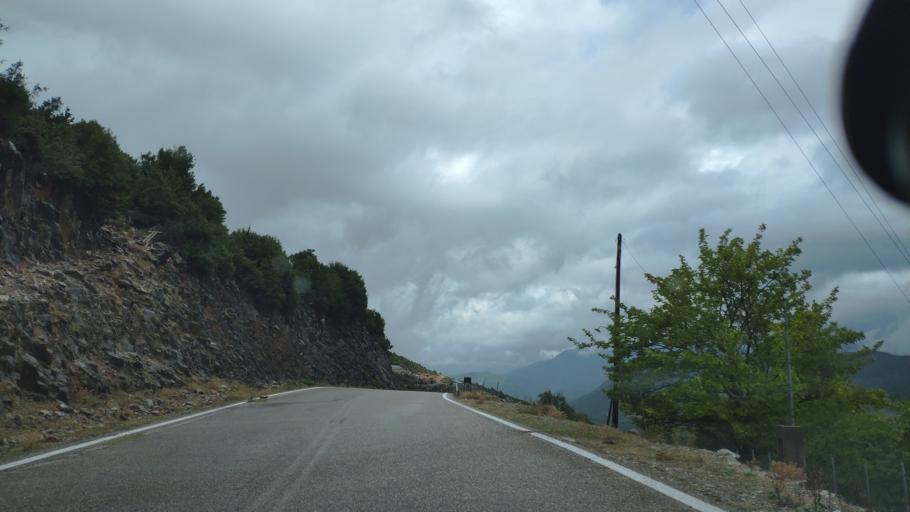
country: GR
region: Thessaly
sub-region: Nomos Kardhitsas
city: Anthiro
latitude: 39.1048
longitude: 21.4090
